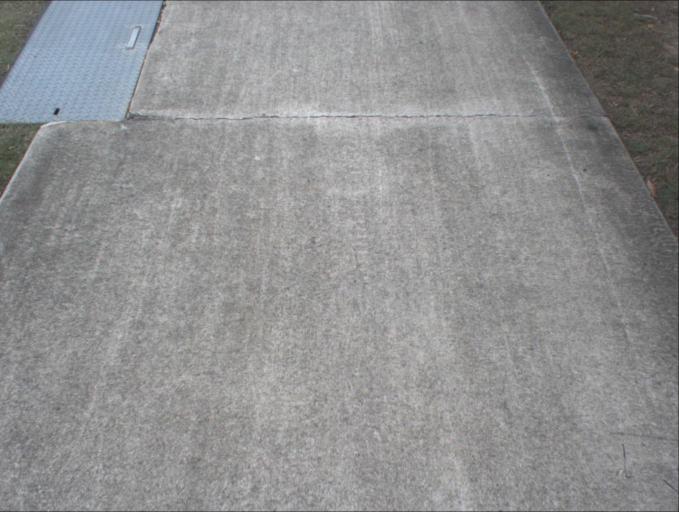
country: AU
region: Queensland
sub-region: Logan
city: Park Ridge South
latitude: -27.6908
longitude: 153.0335
